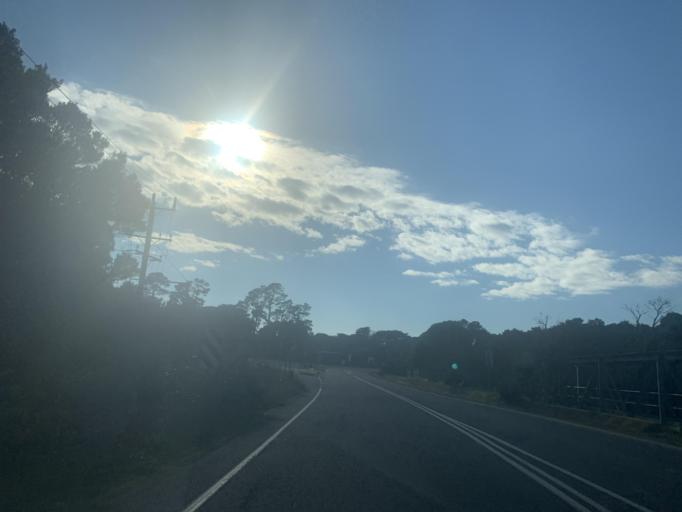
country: AU
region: Victoria
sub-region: Mornington Peninsula
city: Hastings
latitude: -38.2886
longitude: 145.1953
